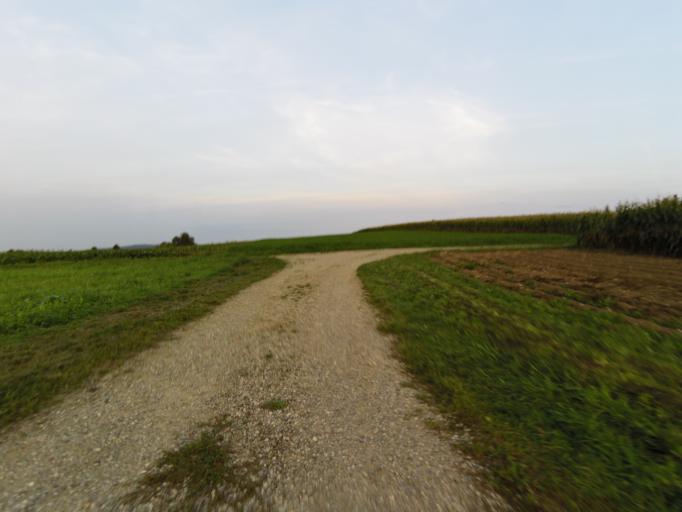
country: CH
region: Thurgau
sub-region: Frauenfeld District
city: Gachnang
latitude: 47.5379
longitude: 8.8703
